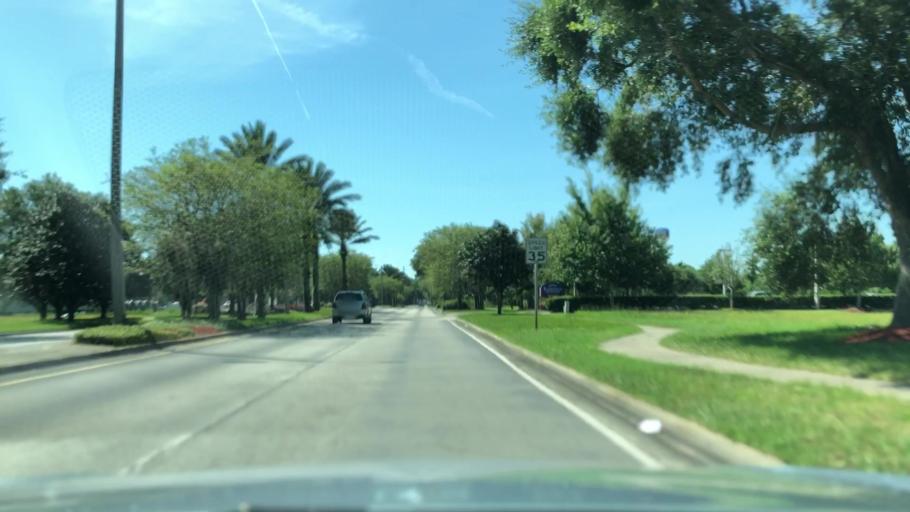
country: US
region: Florida
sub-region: Saint Johns County
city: Saint Augustine
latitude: 29.9207
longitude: -81.4096
